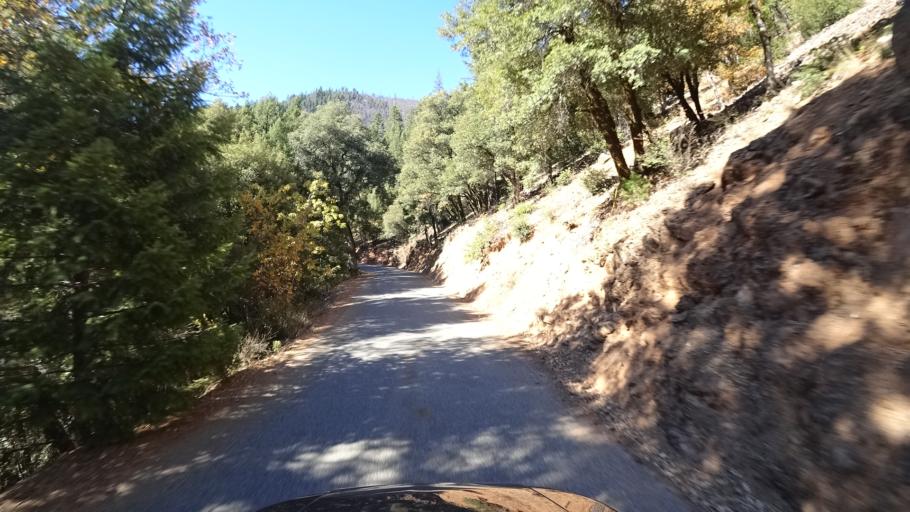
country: US
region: California
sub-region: Siskiyou County
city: Happy Camp
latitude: 41.2965
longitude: -123.1001
